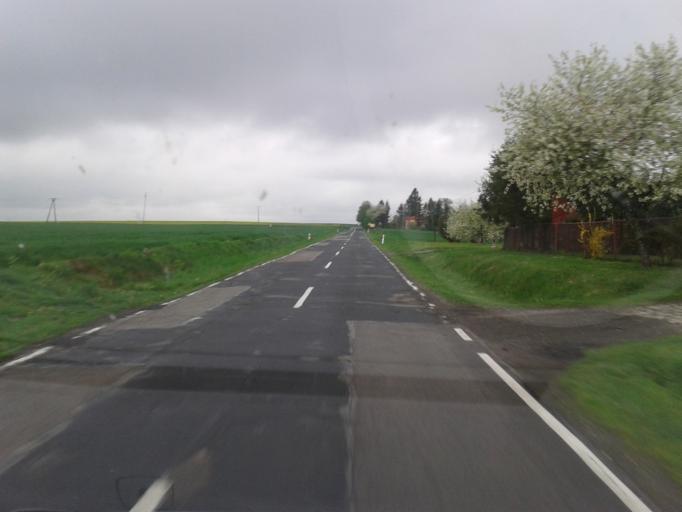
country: PL
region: Lublin Voivodeship
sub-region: Powiat hrubieszowski
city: Dolhobyczow
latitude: 50.5754
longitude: 23.9647
